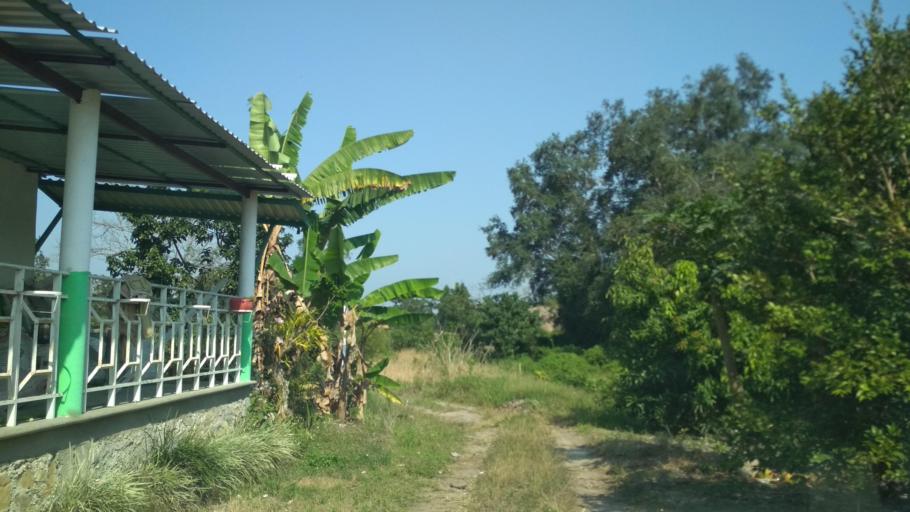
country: MX
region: Puebla
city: San Jose Acateno
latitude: 20.1845
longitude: -97.2572
